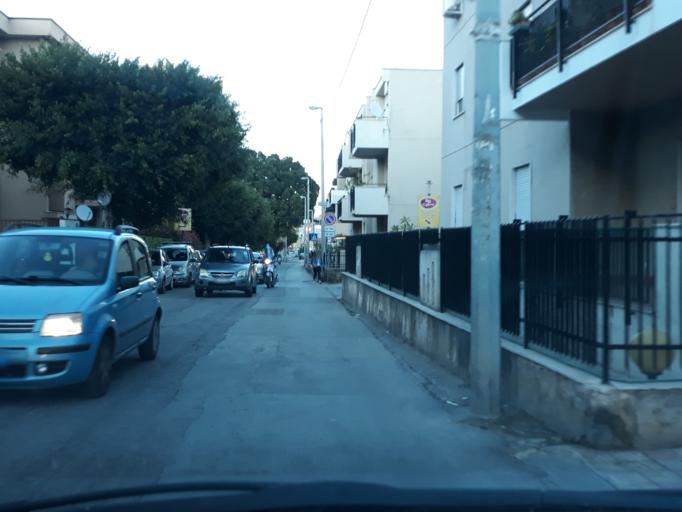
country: IT
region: Sicily
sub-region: Palermo
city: Villa Ciambra
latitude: 38.0918
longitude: 13.3333
